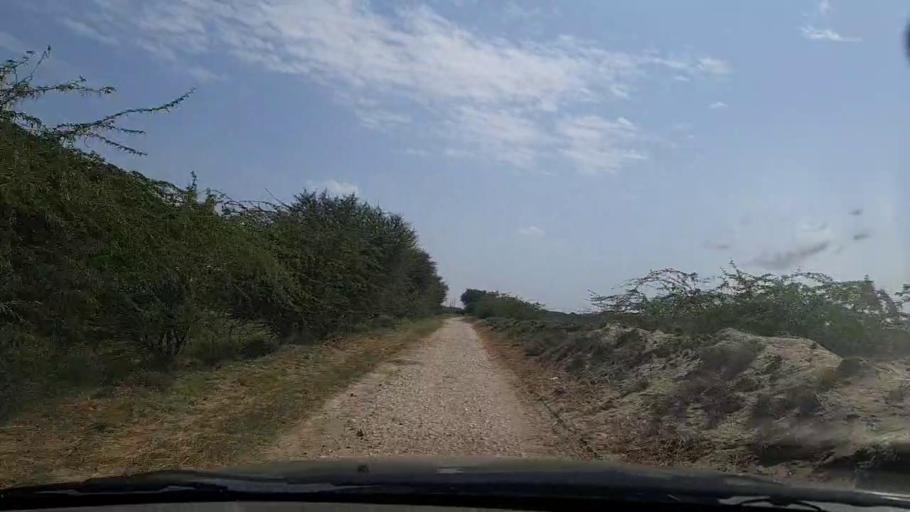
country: PK
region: Sindh
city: Mirpur Batoro
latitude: 24.5711
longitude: 68.1973
